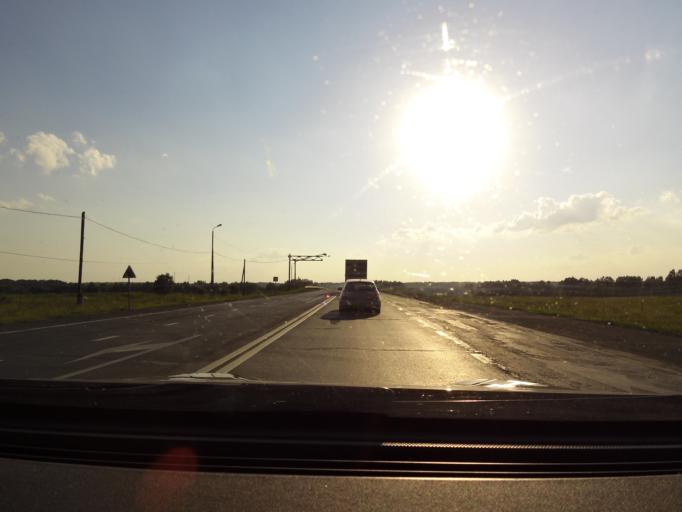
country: RU
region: Sverdlovsk
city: Druzhinino
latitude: 56.8110
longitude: 59.5241
